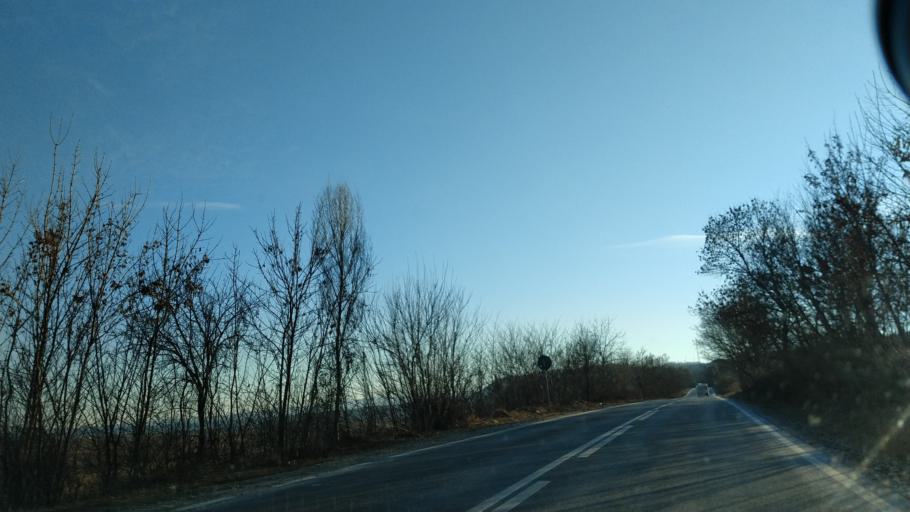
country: RO
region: Bacau
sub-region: Comuna Helegiu
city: Bratila
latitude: 46.3006
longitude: 26.7530
